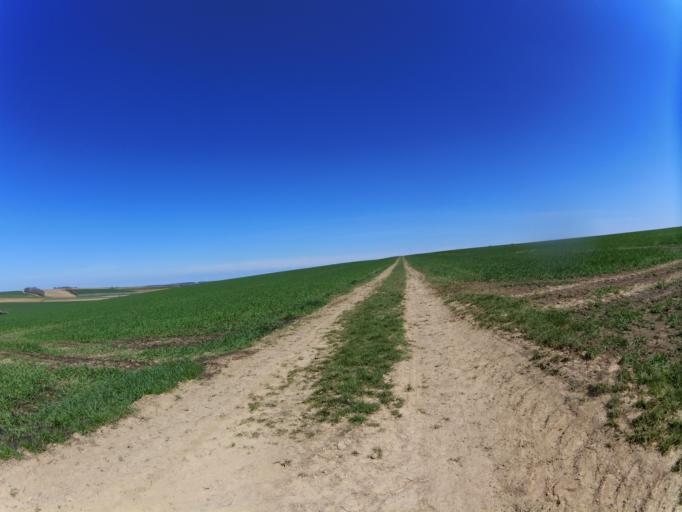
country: DE
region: Bavaria
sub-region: Regierungsbezirk Unterfranken
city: Winterhausen
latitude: 49.6834
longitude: 9.9882
